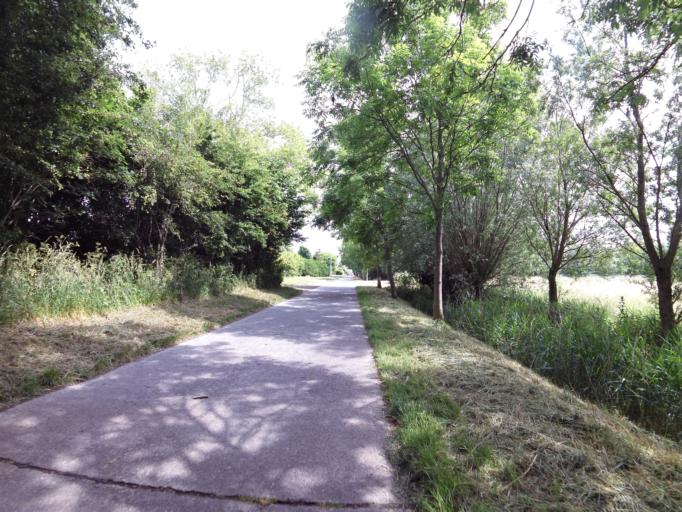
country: BE
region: Flanders
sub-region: Provincie West-Vlaanderen
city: Oudenburg
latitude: 51.1904
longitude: 2.9878
